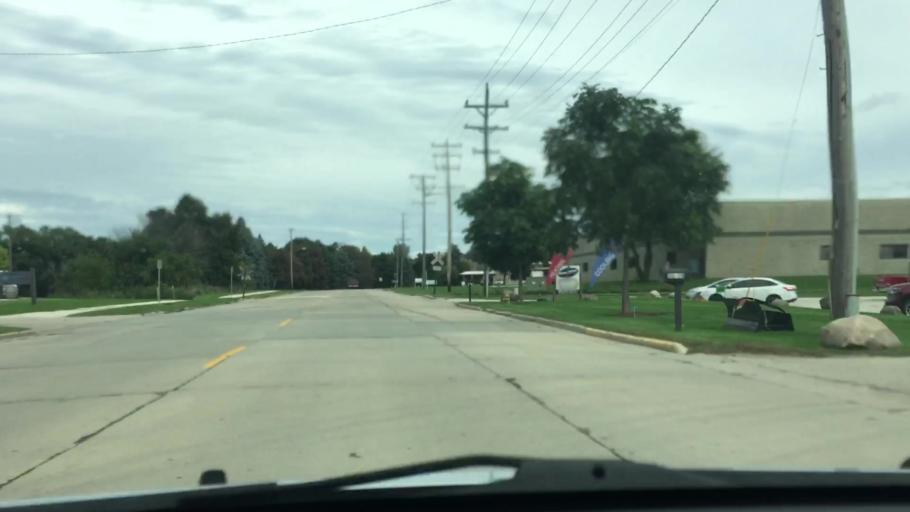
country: US
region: Wisconsin
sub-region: Waukesha County
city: Waukesha
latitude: 42.9999
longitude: -88.2489
